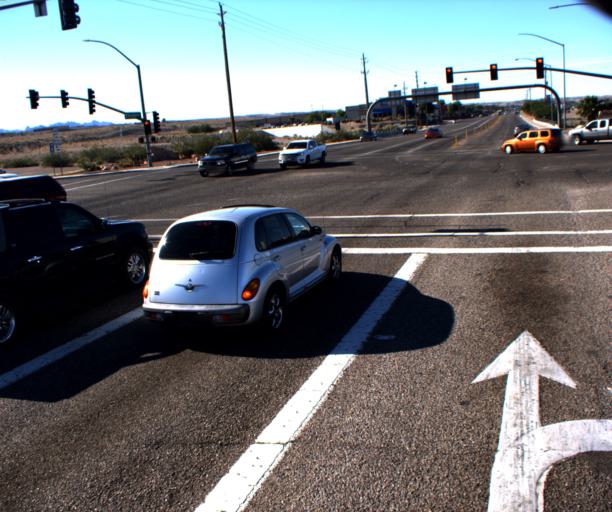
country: US
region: Nevada
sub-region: Clark County
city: Laughlin
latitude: 35.1725
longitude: -114.5660
